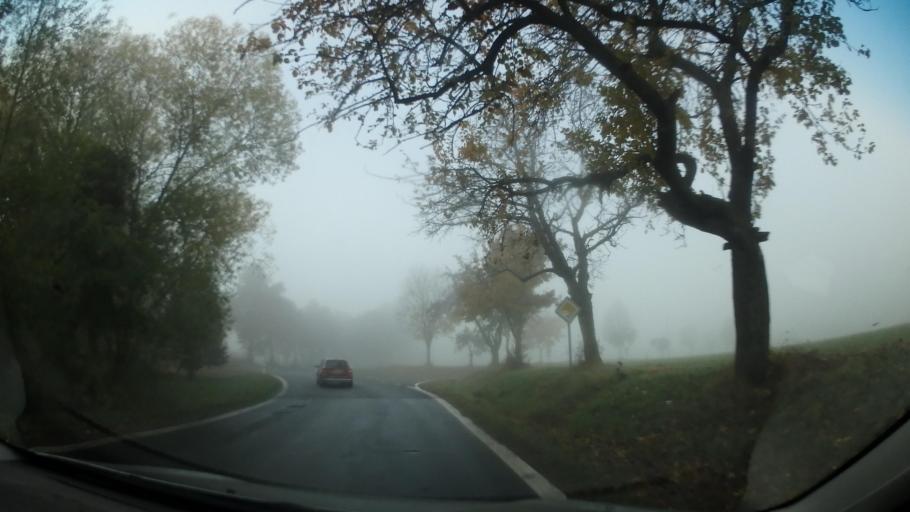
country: CZ
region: Vysocina
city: Krizanov
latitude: 49.4723
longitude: 16.0869
